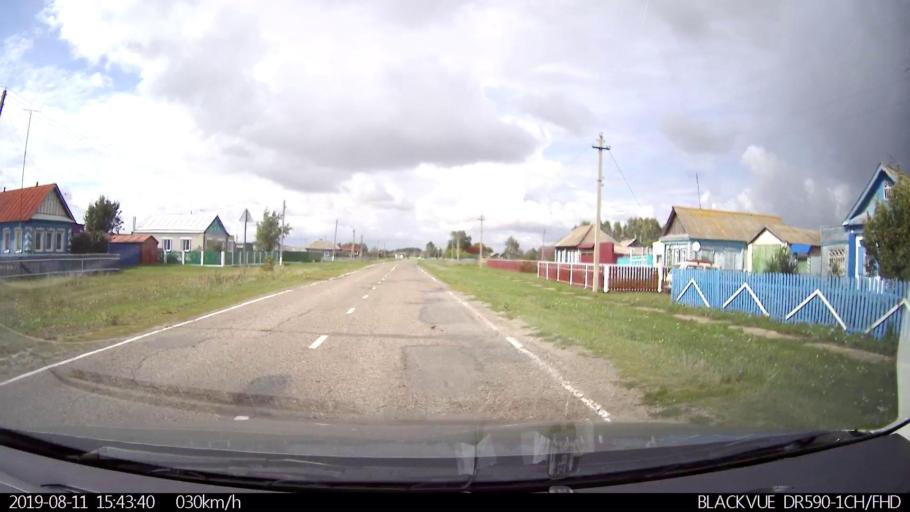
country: RU
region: Ulyanovsk
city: Ignatovka
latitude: 53.8776
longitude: 47.6588
